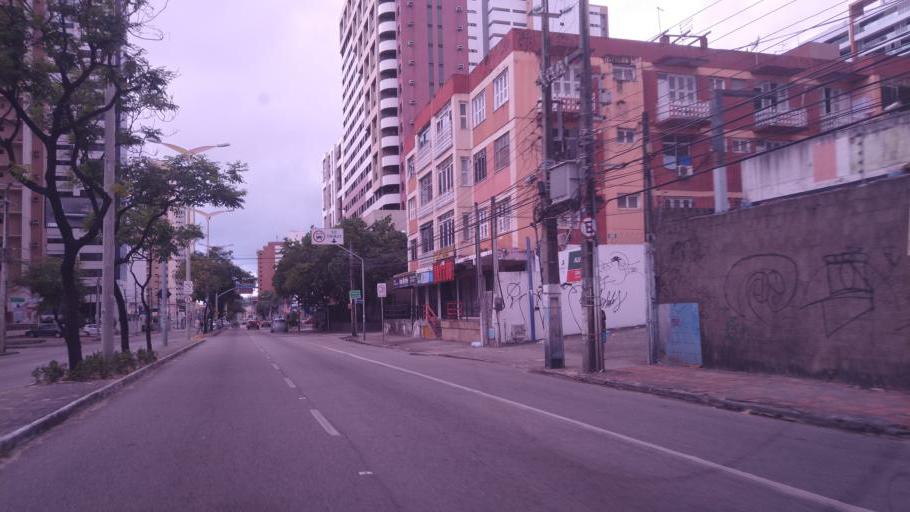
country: BR
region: Ceara
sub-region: Fortaleza
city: Fortaleza
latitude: -3.7267
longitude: -38.4909
